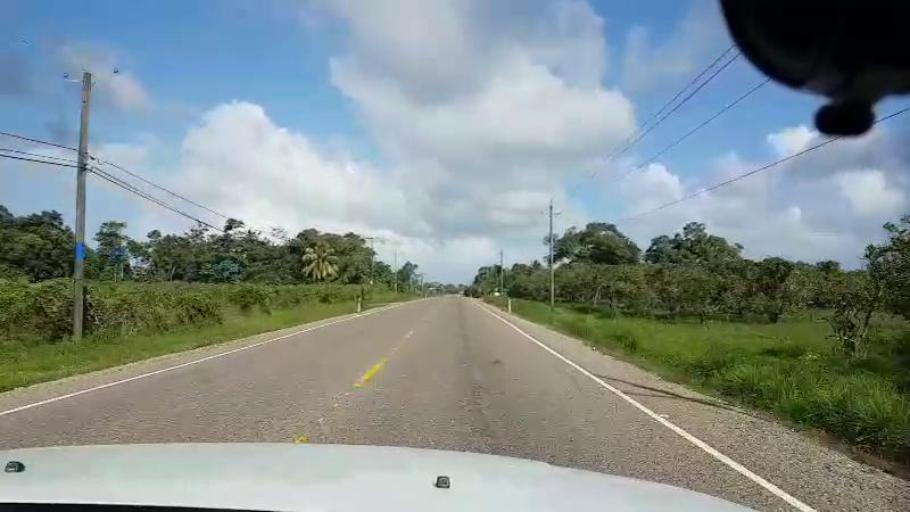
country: BZ
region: Stann Creek
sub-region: Dangriga
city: Dangriga
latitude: 16.9959
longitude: -88.3566
